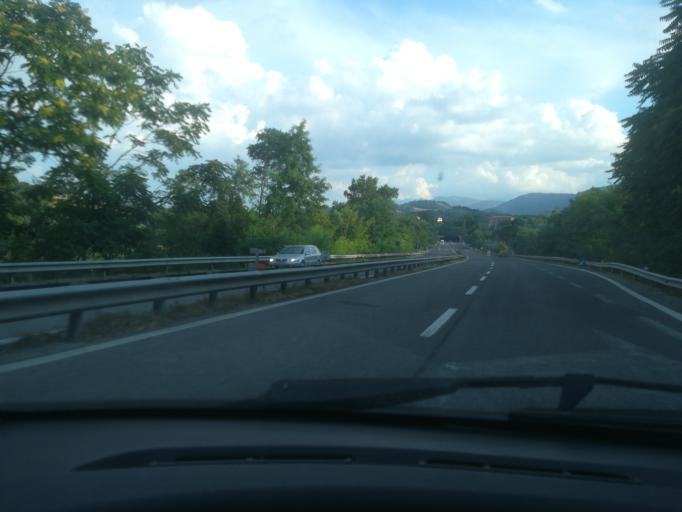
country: IT
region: The Marches
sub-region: Provincia di Macerata
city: Belforte del Chienti
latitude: 43.1693
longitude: 13.2472
